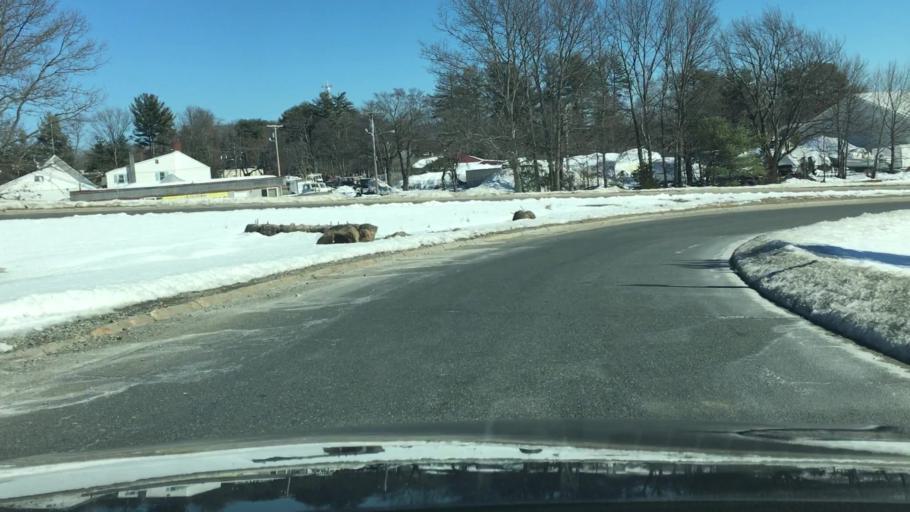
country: US
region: Massachusetts
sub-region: Essex County
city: Amesbury
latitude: 42.8459
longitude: -70.9011
